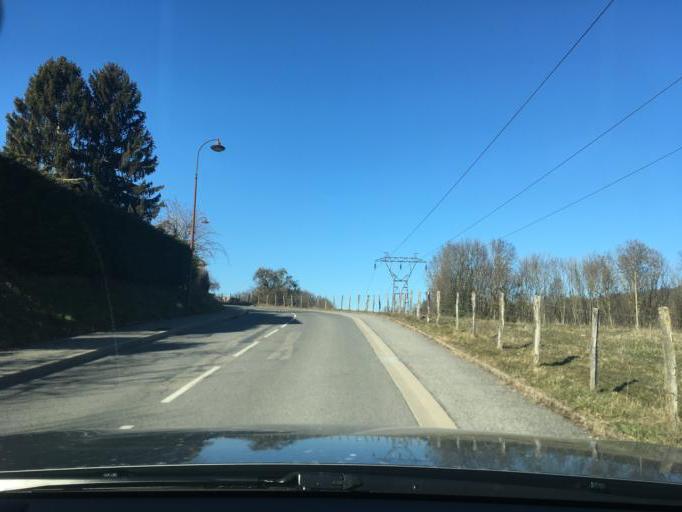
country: FR
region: Rhone-Alpes
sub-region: Departement de la Haute-Savoie
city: Cranves-Sales
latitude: 46.1834
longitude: 6.2950
